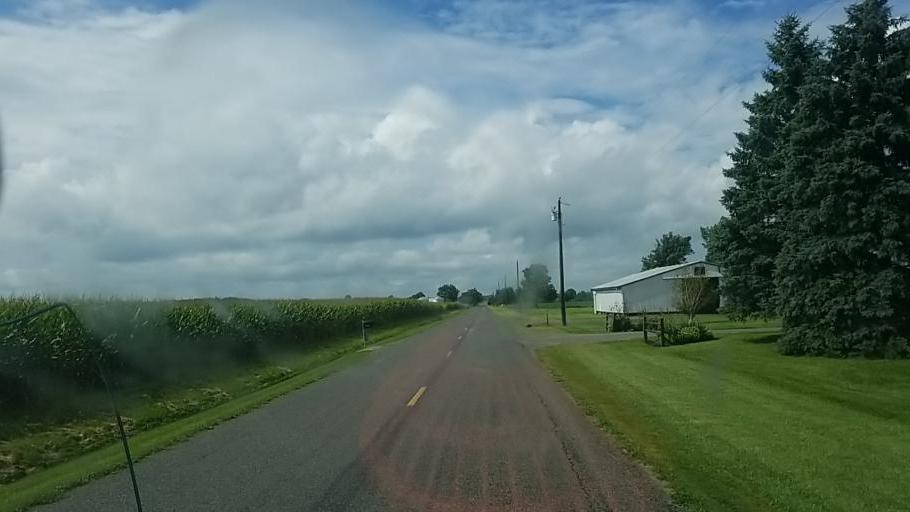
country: US
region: Ohio
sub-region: Hardin County
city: Kenton
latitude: 40.4792
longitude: -83.5113
